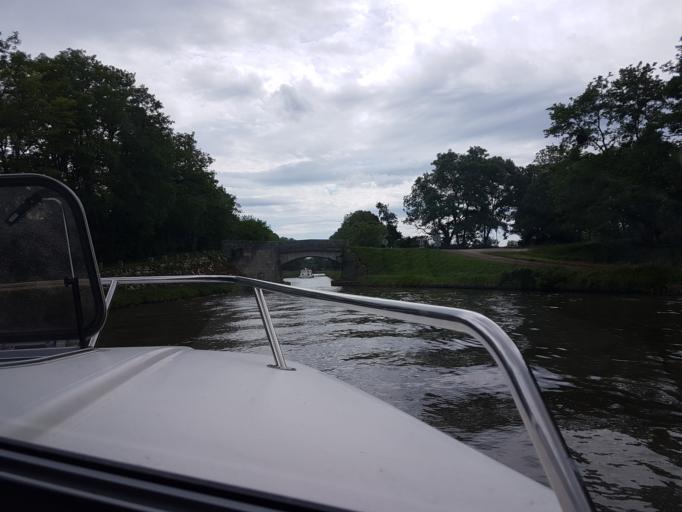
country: FR
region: Bourgogne
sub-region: Departement de la Nievre
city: Clamecy
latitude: 47.4829
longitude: 3.5242
